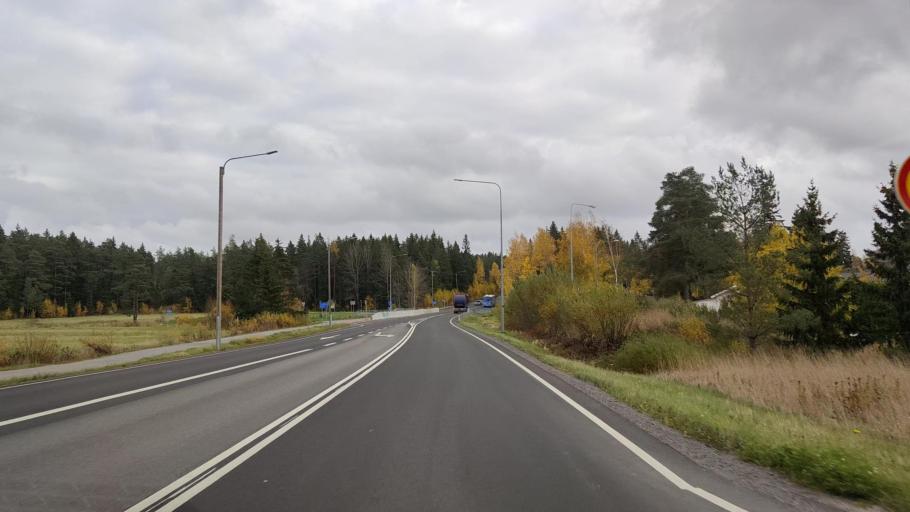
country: FI
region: Varsinais-Suomi
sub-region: Turku
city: Kaarina
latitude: 60.4613
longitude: 22.3587
